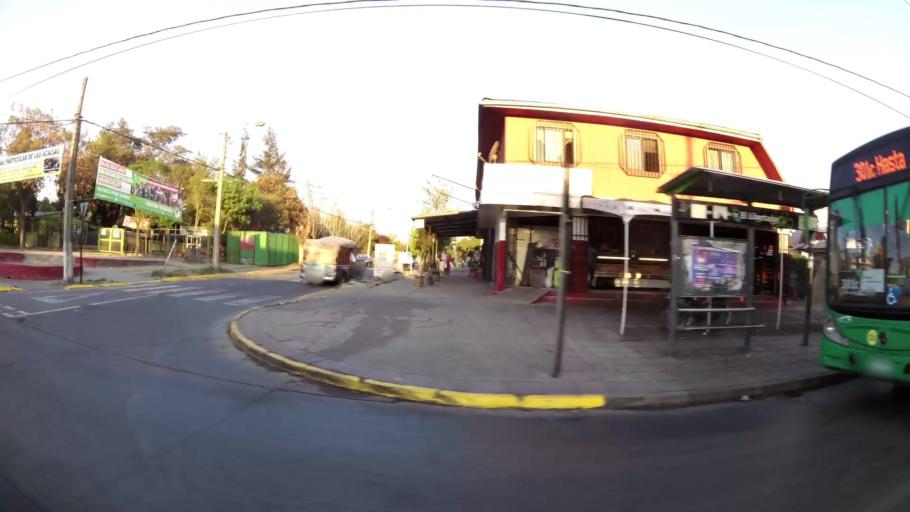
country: CL
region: Santiago Metropolitan
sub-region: Provincia de Maipo
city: San Bernardo
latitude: -33.5689
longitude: -70.6728
